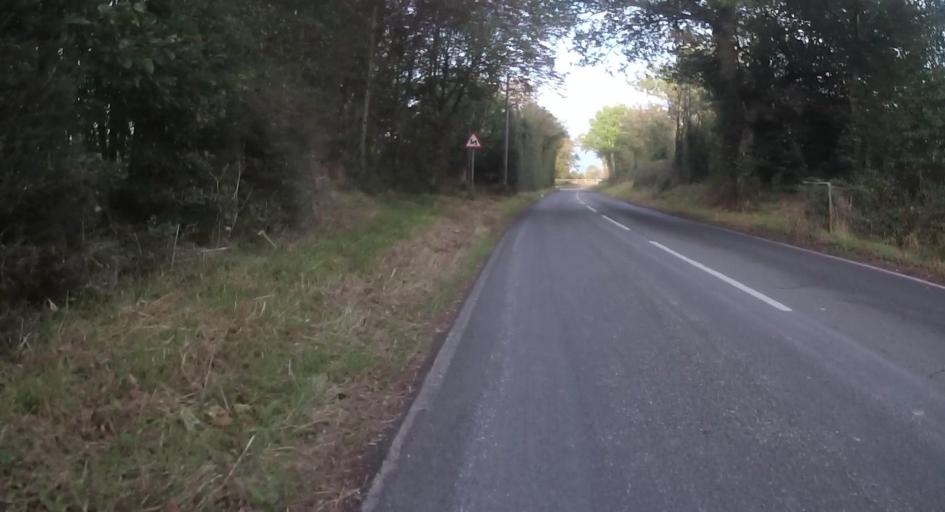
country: GB
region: England
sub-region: Hampshire
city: Tadley
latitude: 51.3804
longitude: -1.1689
